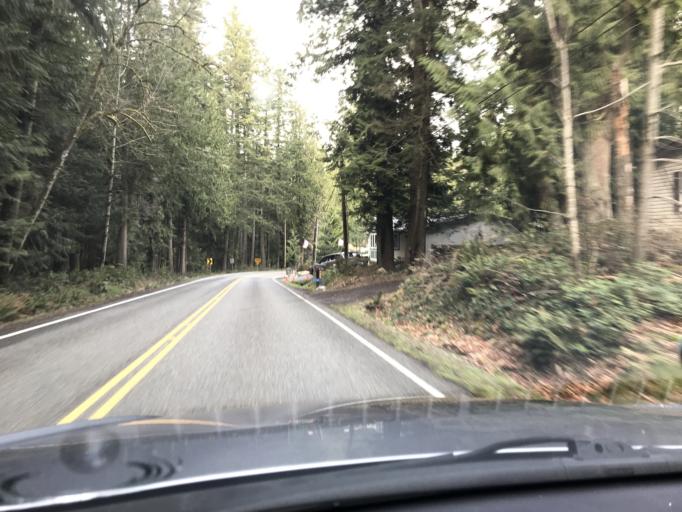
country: US
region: Washington
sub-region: King County
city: Ames Lake
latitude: 47.6400
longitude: -121.9681
